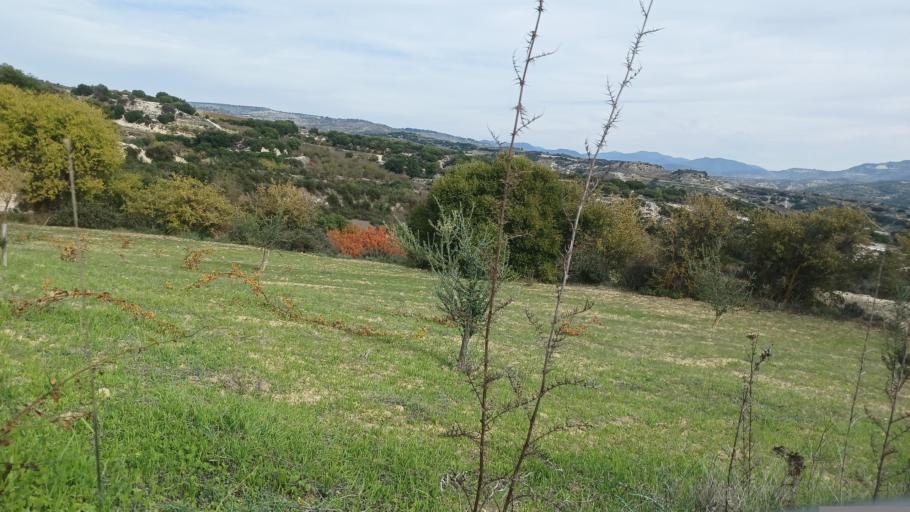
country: CY
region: Pafos
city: Mesogi
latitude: 34.8618
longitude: 32.5275
